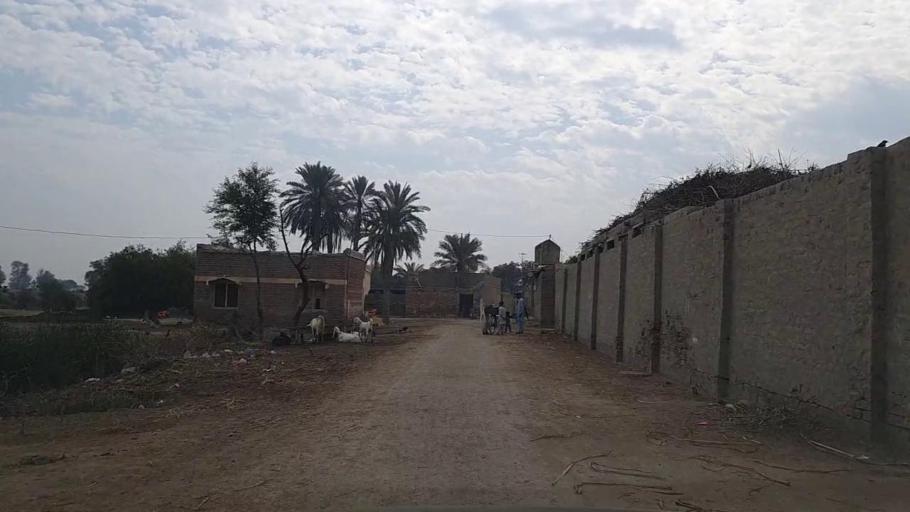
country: PK
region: Sindh
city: Daur
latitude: 26.3902
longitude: 68.3603
